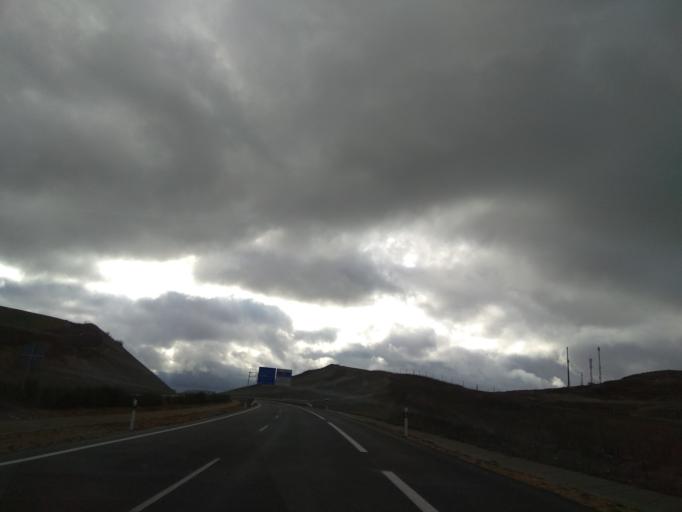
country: ES
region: Castille and Leon
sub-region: Provincia de Burgos
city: Sotragero
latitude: 42.3952
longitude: -3.6985
